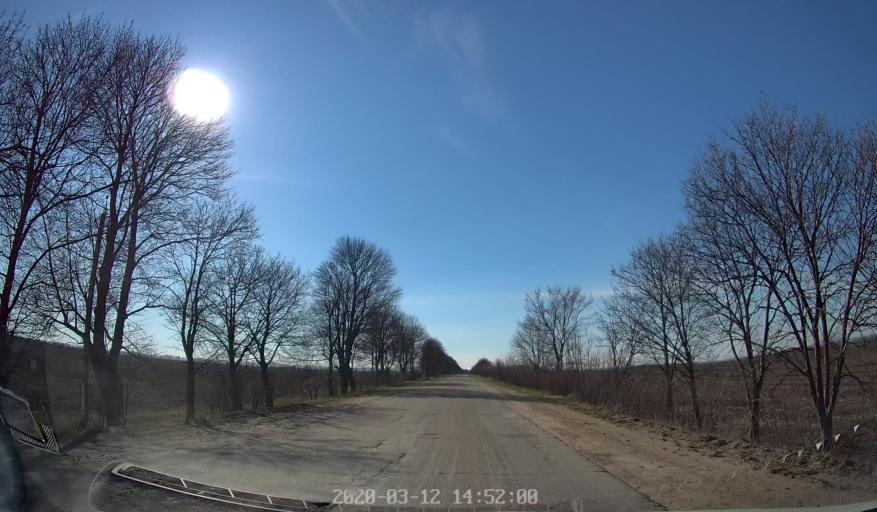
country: MD
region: Criuleni
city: Criuleni
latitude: 47.2210
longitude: 29.1065
